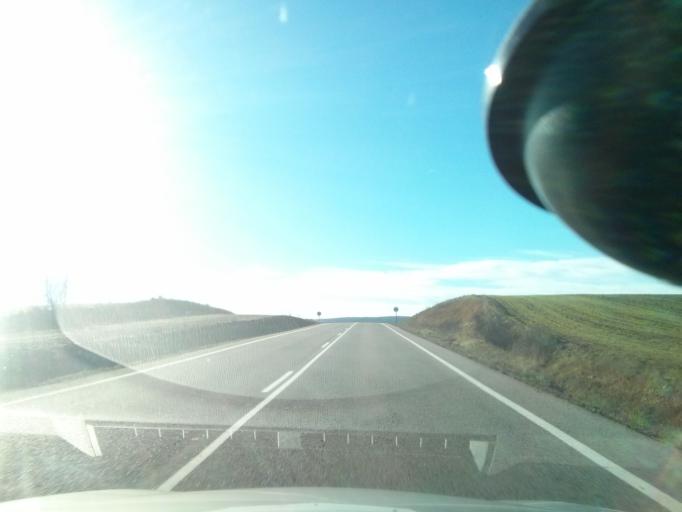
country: ES
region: Castille and Leon
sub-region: Provincia de Burgos
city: Quintanaortuno
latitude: 42.5346
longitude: -3.6485
